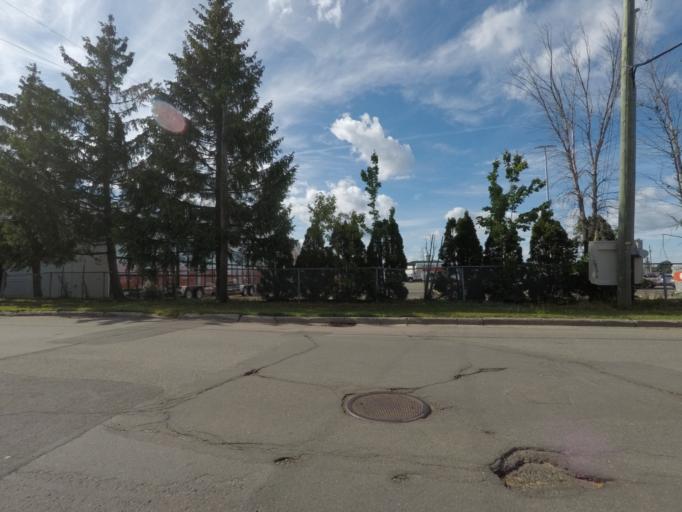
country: CA
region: New Brunswick
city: Moncton
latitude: 46.1044
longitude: -64.8226
